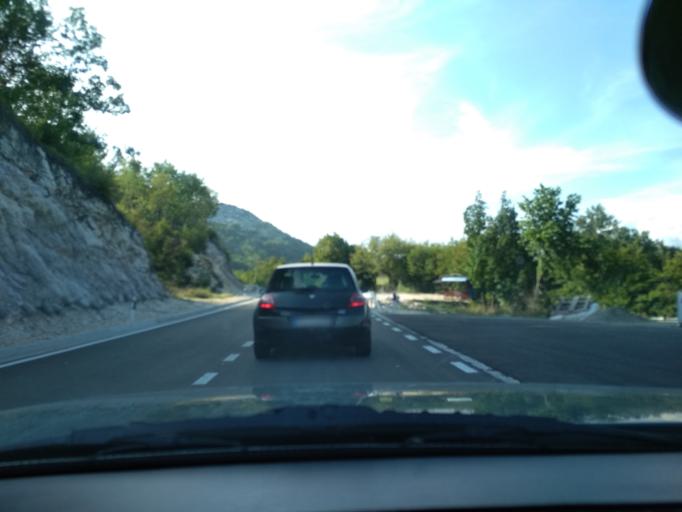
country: ME
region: Cetinje
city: Cetinje
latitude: 42.4166
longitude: 18.8792
